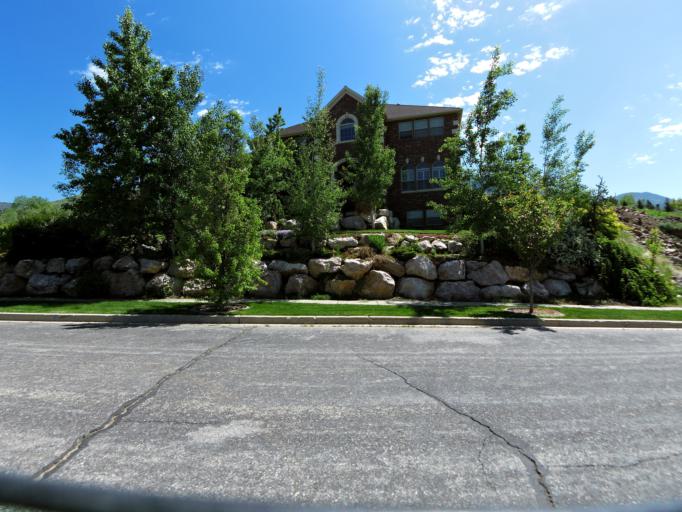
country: US
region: Utah
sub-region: Weber County
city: Uintah
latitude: 41.1752
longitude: -111.9390
